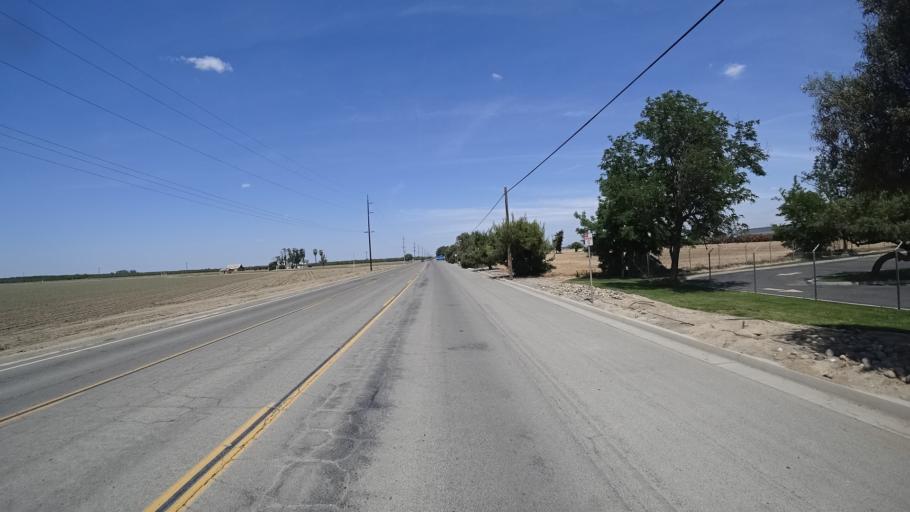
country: US
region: California
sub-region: Kings County
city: Home Garden
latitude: 36.2813
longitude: -119.6548
